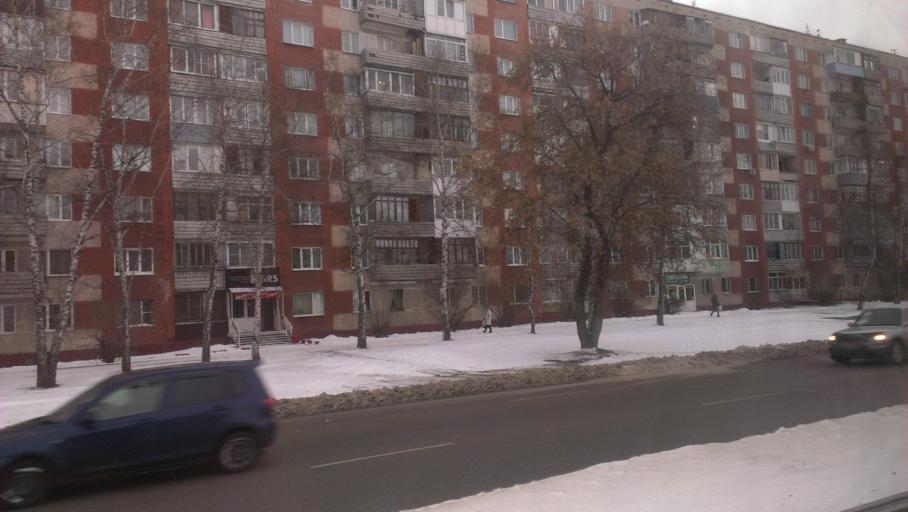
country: RU
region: Altai Krai
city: Novosilikatnyy
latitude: 53.3683
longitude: 83.6771
